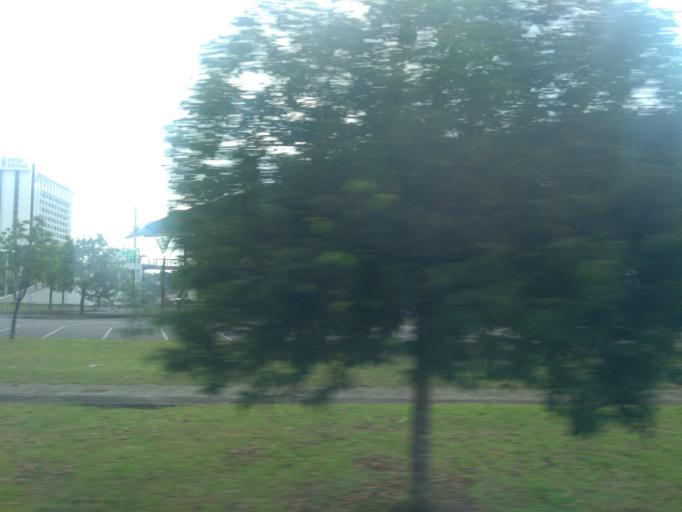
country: MY
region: Sarawak
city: Kuching
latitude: 1.5624
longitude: 110.4042
